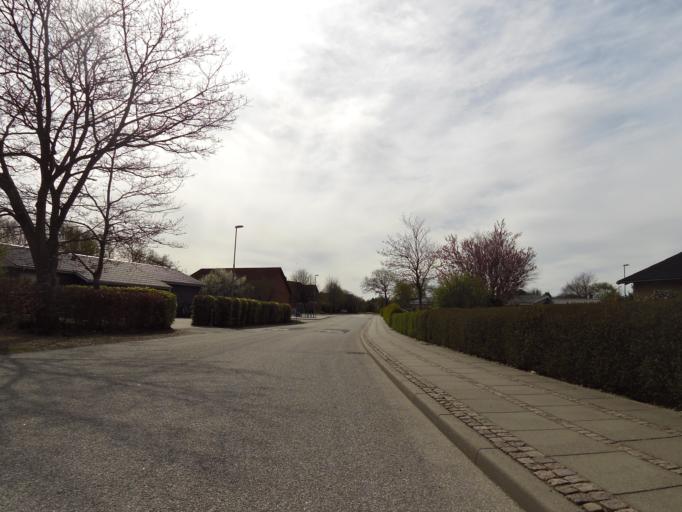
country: DK
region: Central Jutland
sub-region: Skive Kommune
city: Skive
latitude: 56.5354
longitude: 8.9418
